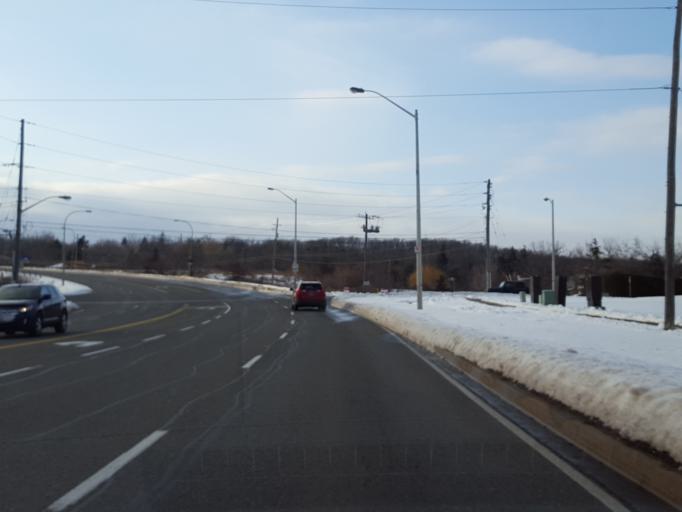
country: CA
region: Ontario
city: Burlington
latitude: 43.3629
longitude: -79.8517
